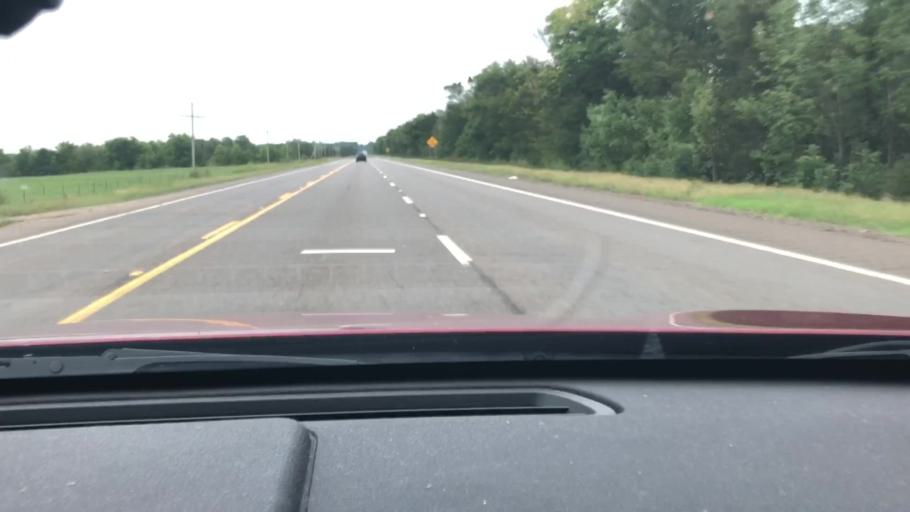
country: US
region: Arkansas
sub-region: Lafayette County
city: Lewisville
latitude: 33.3565
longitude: -93.6497
